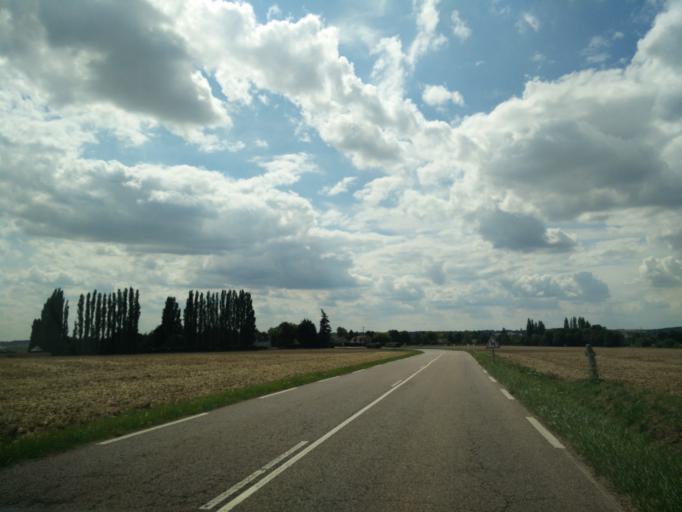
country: FR
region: Ile-de-France
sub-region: Departement des Yvelines
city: Guerville
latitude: 48.9187
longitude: 1.7310
